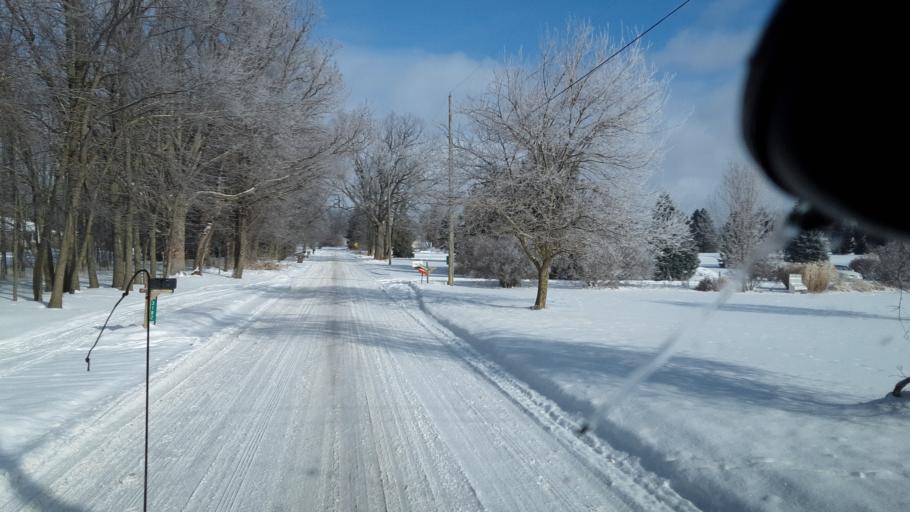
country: US
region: Michigan
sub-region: Eaton County
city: Eaton Rapids
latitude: 42.5211
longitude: -84.6309
